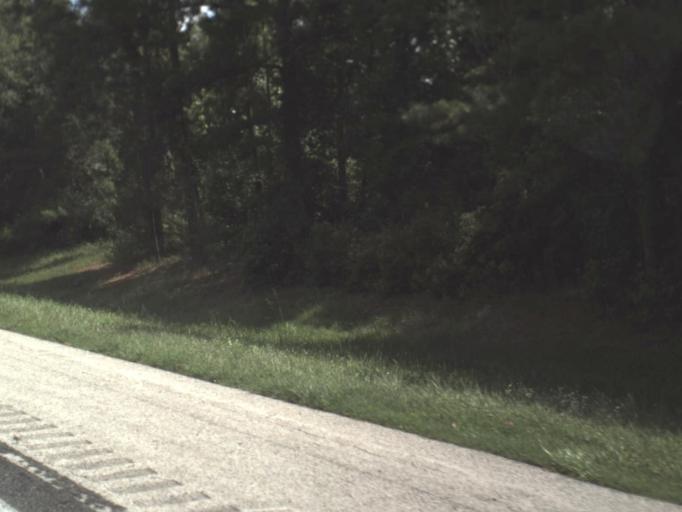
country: US
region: Florida
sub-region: Alachua County
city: High Springs
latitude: 29.7905
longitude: -82.5151
